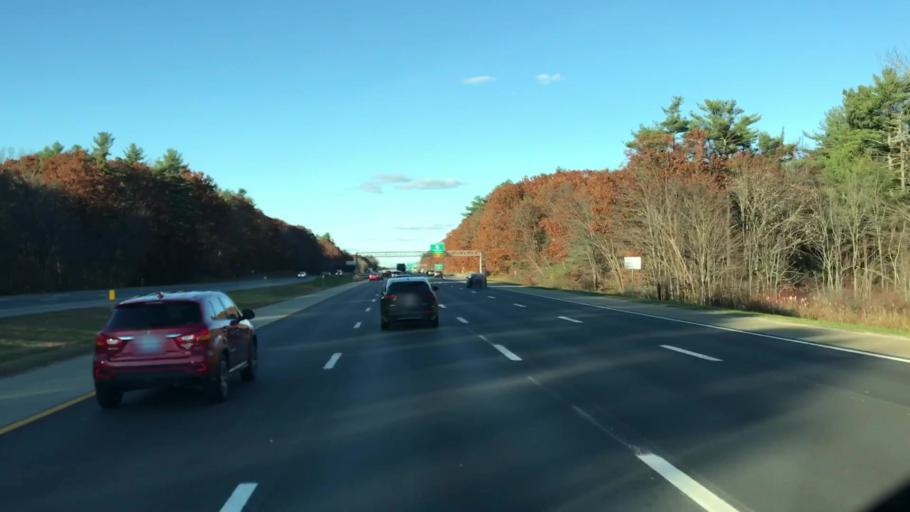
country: US
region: New Hampshire
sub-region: Rockingham County
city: Hampton
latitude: 42.9433
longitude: -70.8600
